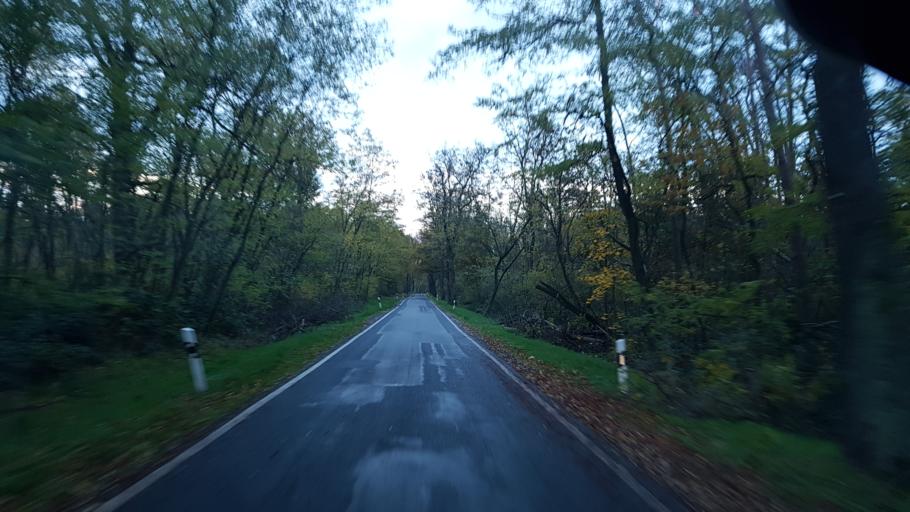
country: DE
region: Brandenburg
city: Muhlberg
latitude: 51.4850
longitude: 13.2301
